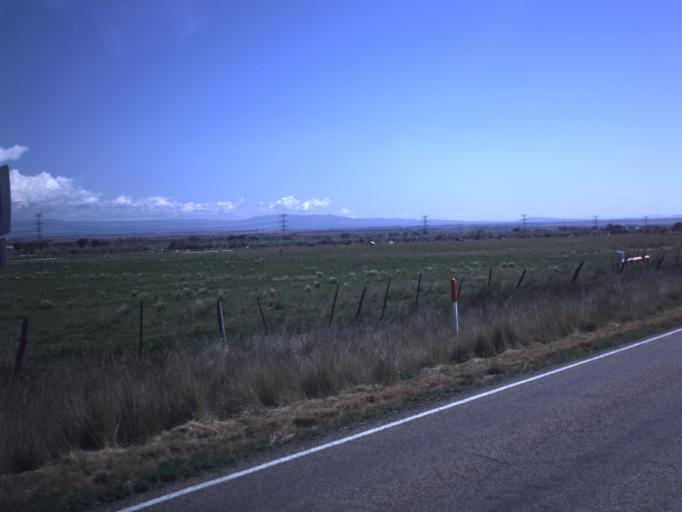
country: US
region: Utah
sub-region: Duchesne County
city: Roosevelt
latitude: 40.2584
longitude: -110.1011
